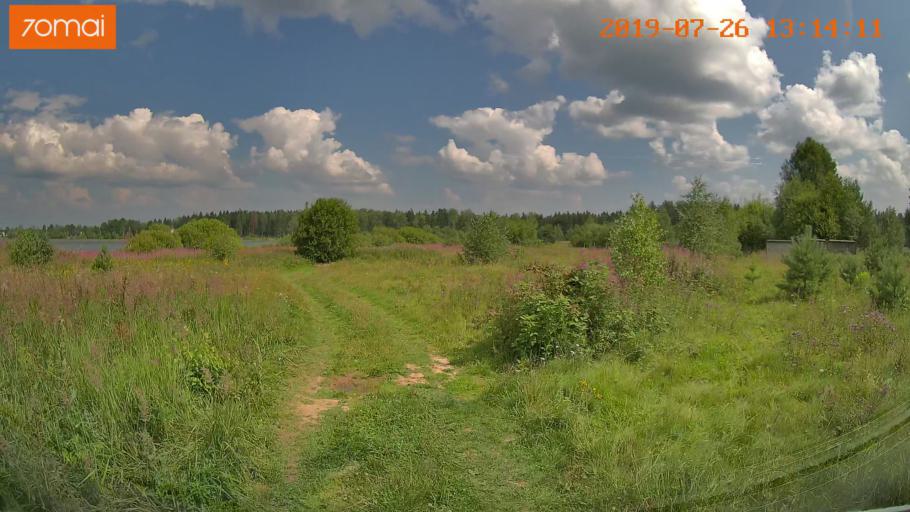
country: RU
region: Ivanovo
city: Bogorodskoye
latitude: 57.0571
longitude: 41.0595
